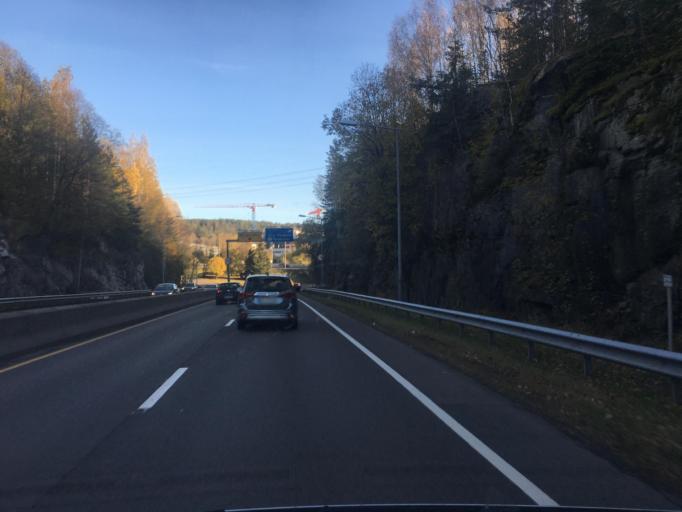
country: NO
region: Akershus
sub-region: Lorenskog
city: Kjenn
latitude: 59.9492
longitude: 10.9436
